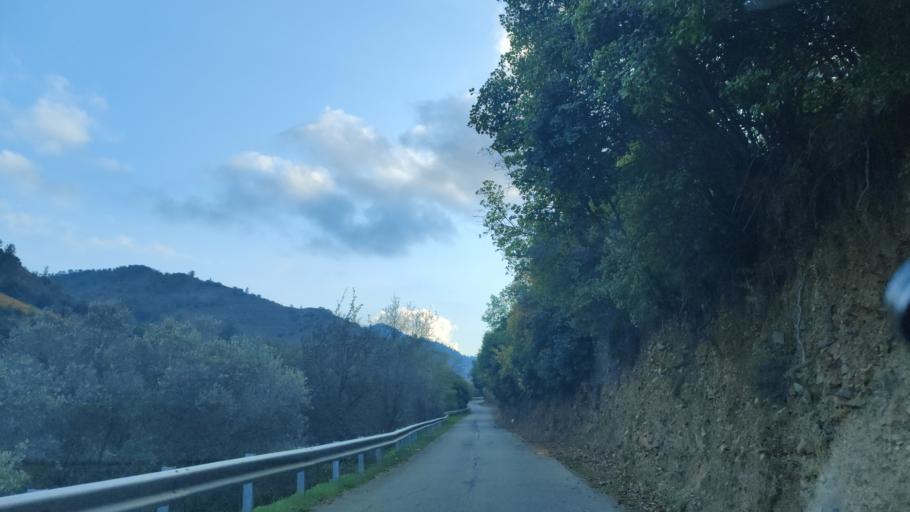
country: CY
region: Lefkosia
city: Lefka
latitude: 35.0479
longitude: 32.7357
